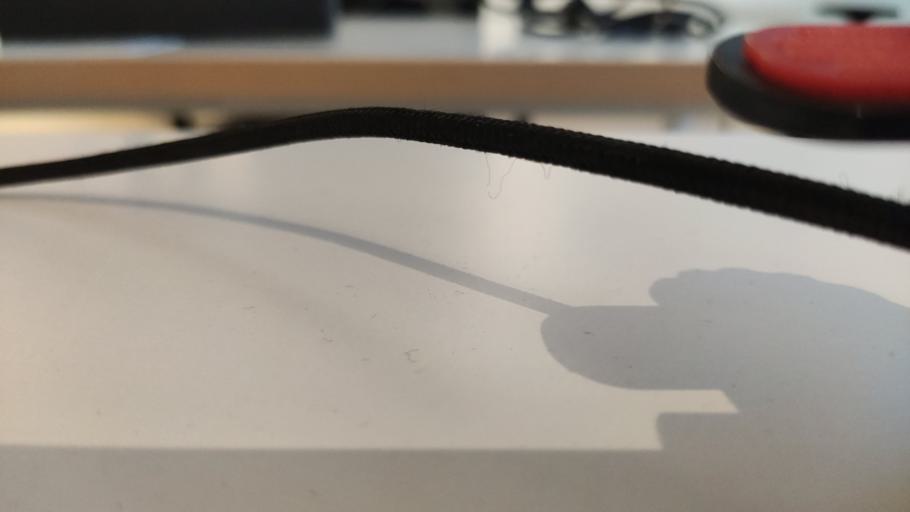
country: RU
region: Moskovskaya
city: Sychevo
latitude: 55.8386
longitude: 36.3327
